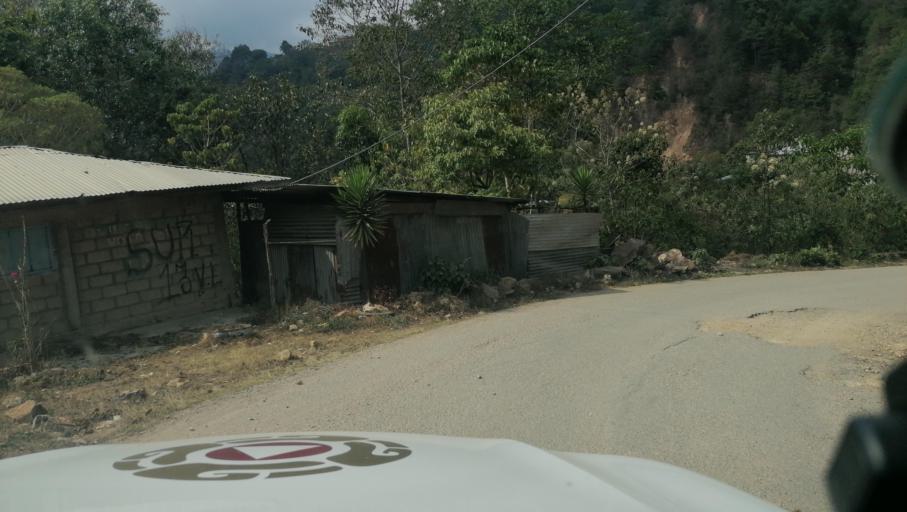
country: GT
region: San Marcos
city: Tacana
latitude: 15.2119
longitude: -92.1973
